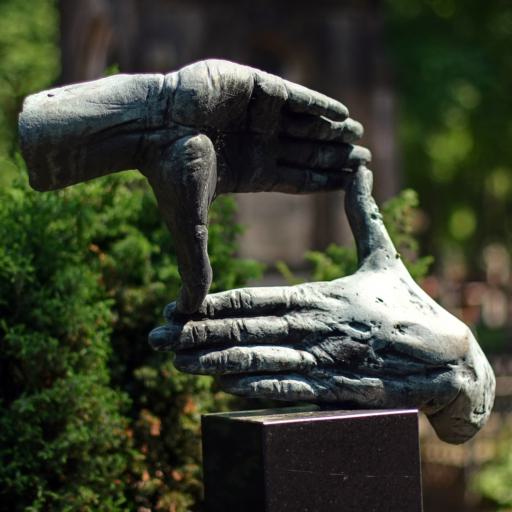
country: PL
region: Masovian Voivodeship
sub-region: Warszawa
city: Wola
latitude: 52.2535
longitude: 20.9749
